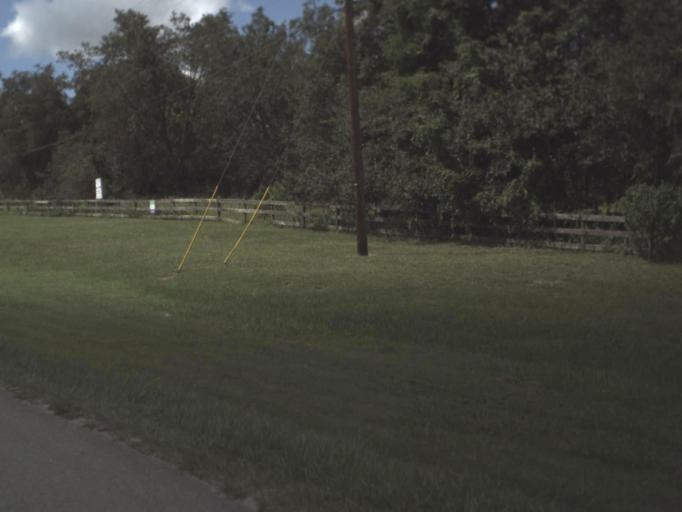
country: US
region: Florida
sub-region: Polk County
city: Polk City
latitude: 28.1897
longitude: -81.8207
